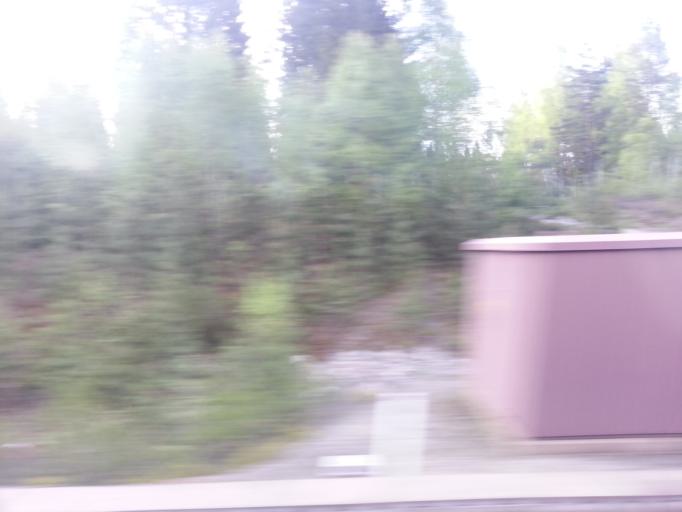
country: NO
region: Akershus
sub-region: Nannestad
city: Maura
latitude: 60.2110
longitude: 11.1071
